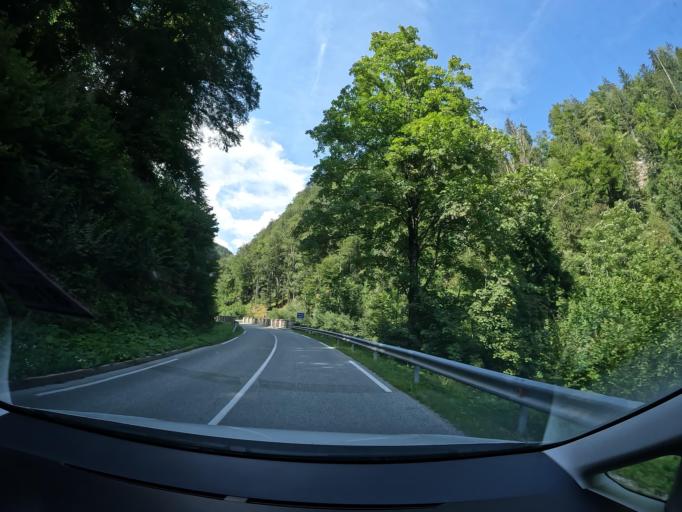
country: SI
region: Trzic
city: Trzic
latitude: 46.3902
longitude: 14.3551
